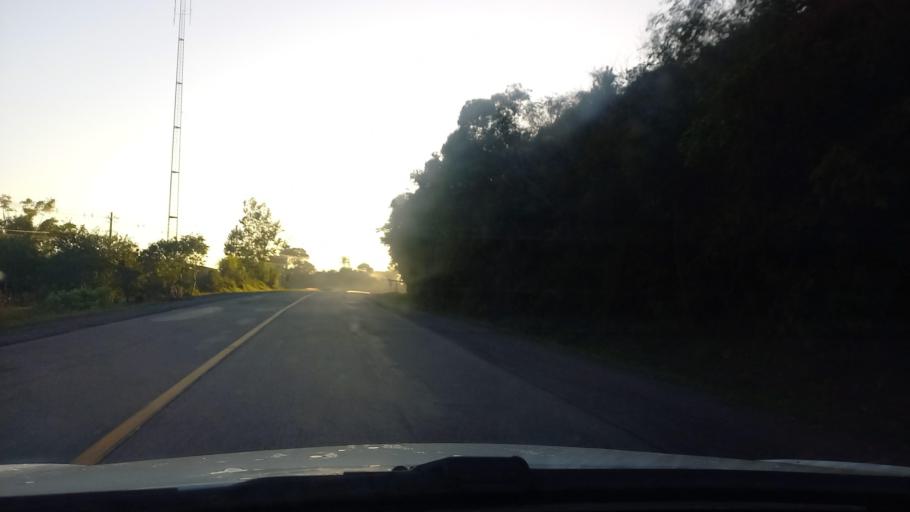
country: BR
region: Rio Grande do Sul
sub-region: Candelaria
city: Candelaria
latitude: -29.6824
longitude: -52.8431
